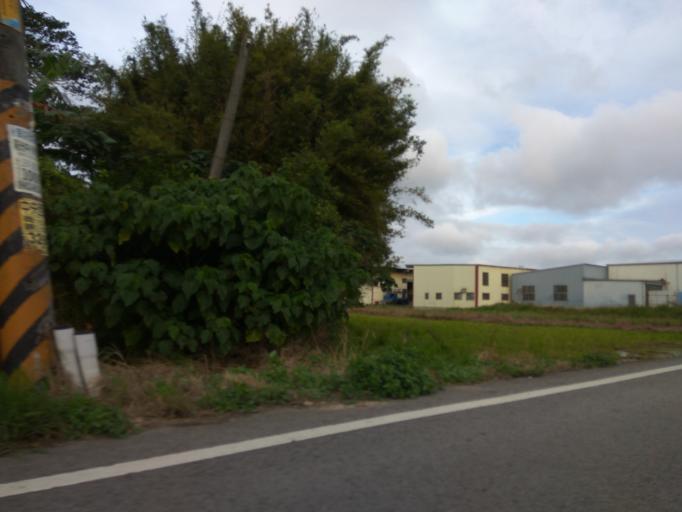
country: TW
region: Taiwan
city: Daxi
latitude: 24.9220
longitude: 121.1928
